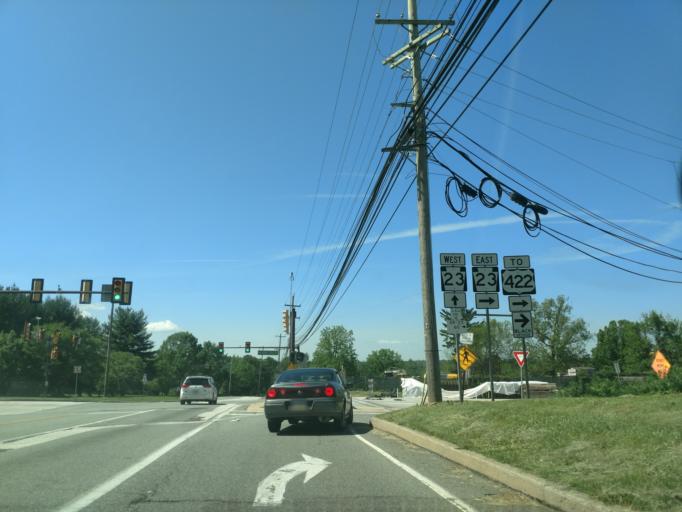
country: US
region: Pennsylvania
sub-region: Montgomery County
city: King of Prussia
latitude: 40.1004
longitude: -75.4201
